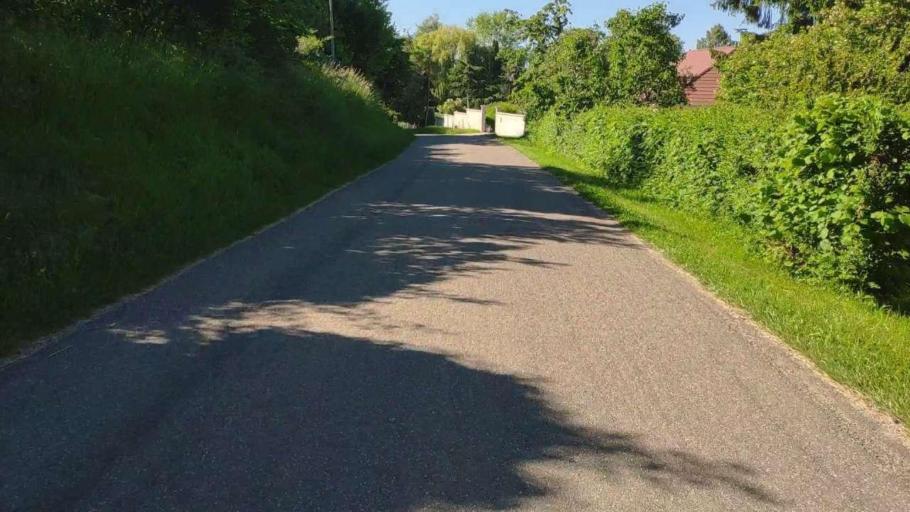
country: FR
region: Franche-Comte
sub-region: Departement du Jura
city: Montmorot
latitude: 46.7219
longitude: 5.5515
